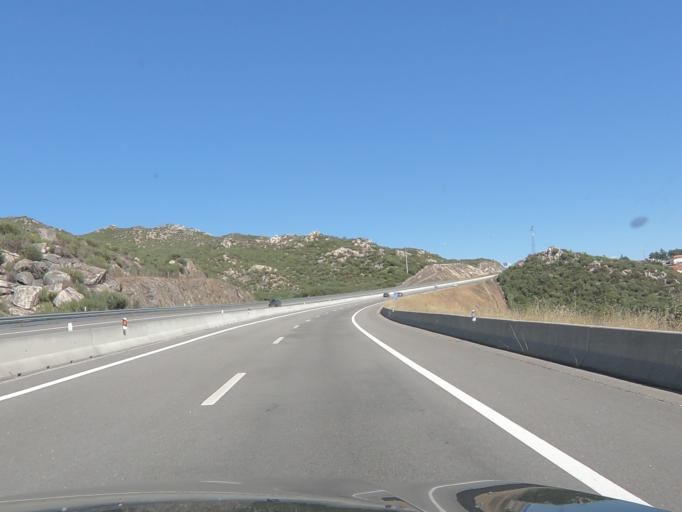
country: PT
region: Vila Real
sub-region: Murca
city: Murca
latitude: 41.3757
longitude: -7.5263
